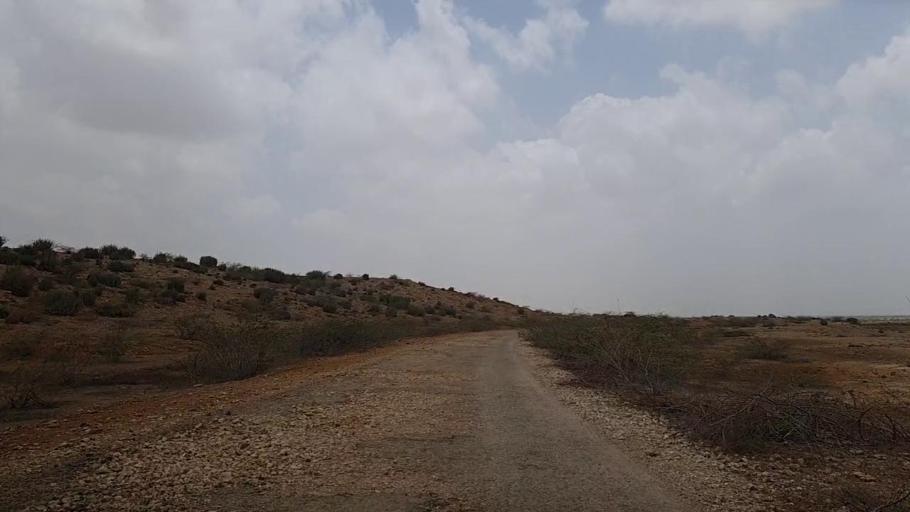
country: PK
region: Sindh
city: Thatta
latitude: 24.8951
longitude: 67.8970
